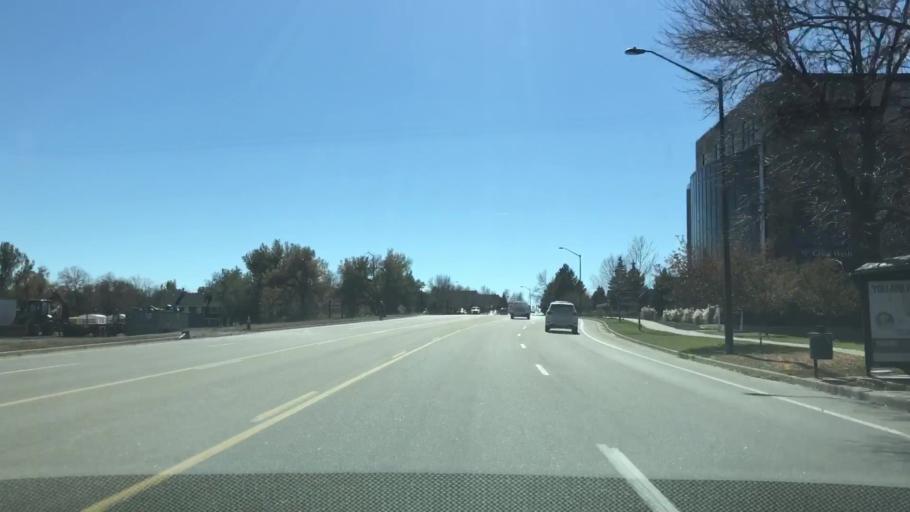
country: US
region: Colorado
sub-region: Larimer County
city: Fort Collins
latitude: 40.5368
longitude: -105.0737
